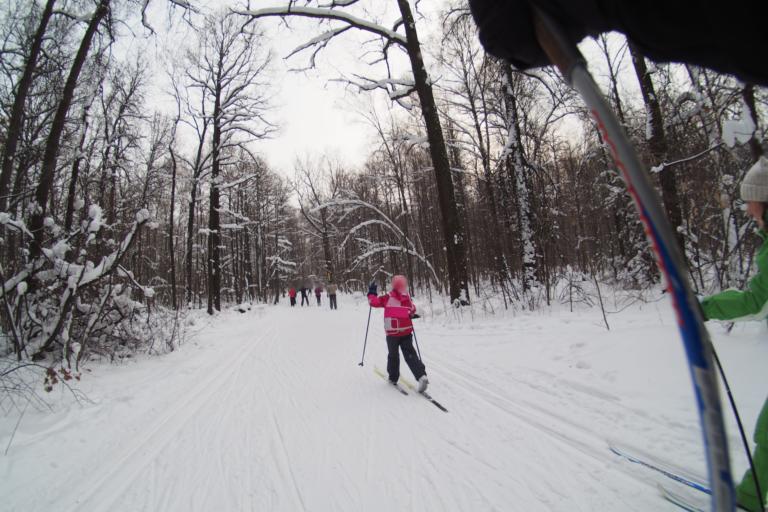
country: RU
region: Moskovskaya
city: Izmaylovo
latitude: 55.7670
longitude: 37.7775
